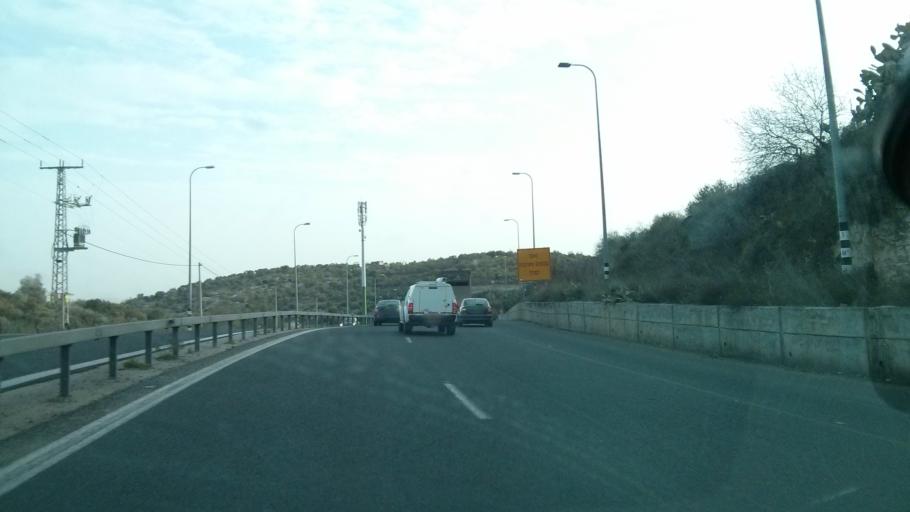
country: IL
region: Haifa
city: Umm el Fahm
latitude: 32.5574
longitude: 35.1697
